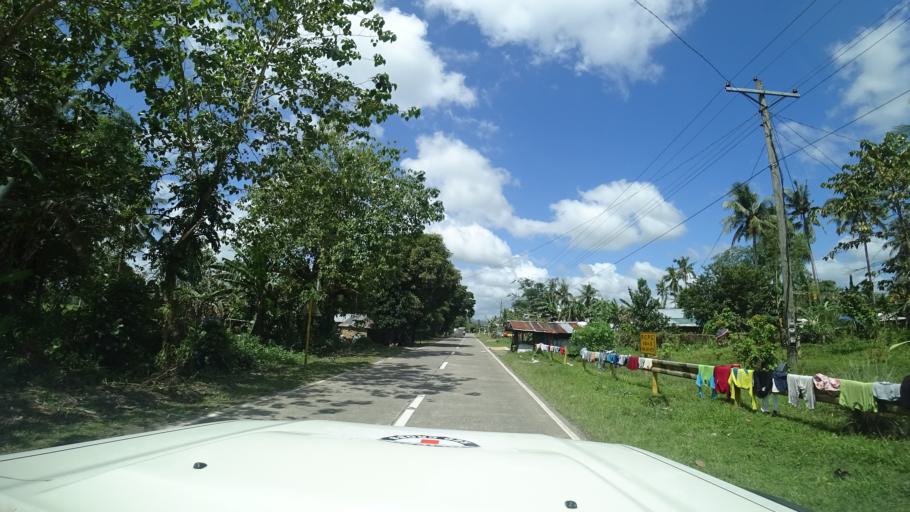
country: PH
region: Eastern Visayas
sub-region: Province of Leyte
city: Mayorga
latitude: 10.9039
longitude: 124.9900
